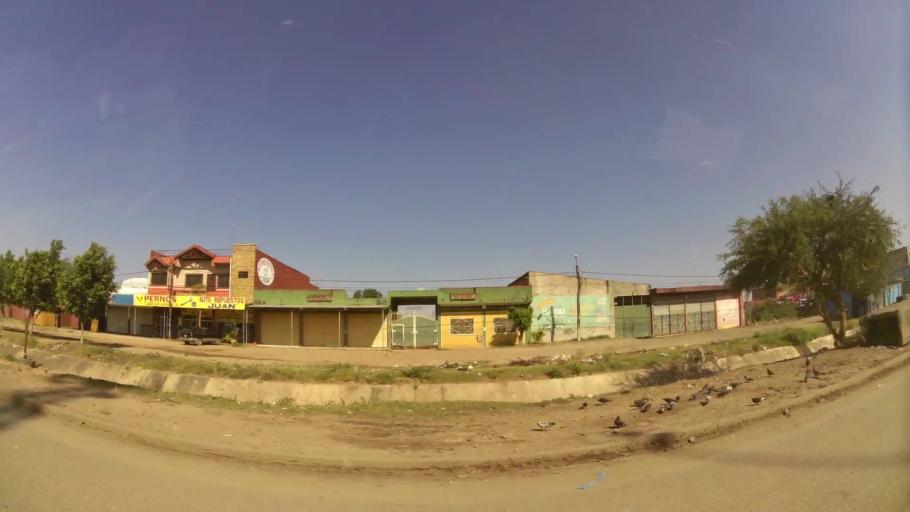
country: BO
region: Santa Cruz
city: Cotoca
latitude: -17.8166
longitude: -63.1153
